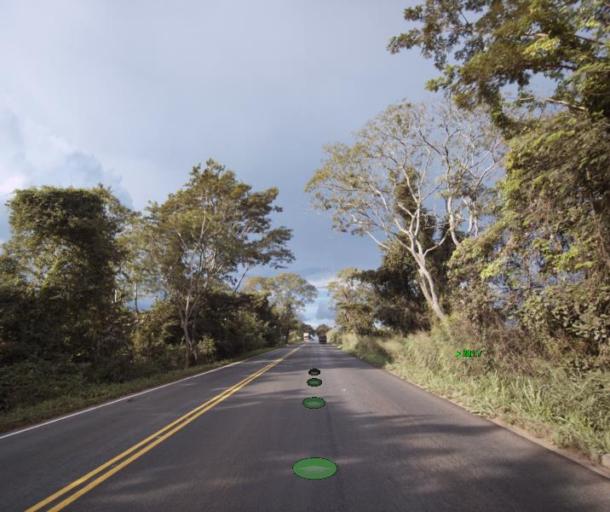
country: BR
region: Goias
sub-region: Ceres
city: Ceres
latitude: -15.1489
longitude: -49.5344
